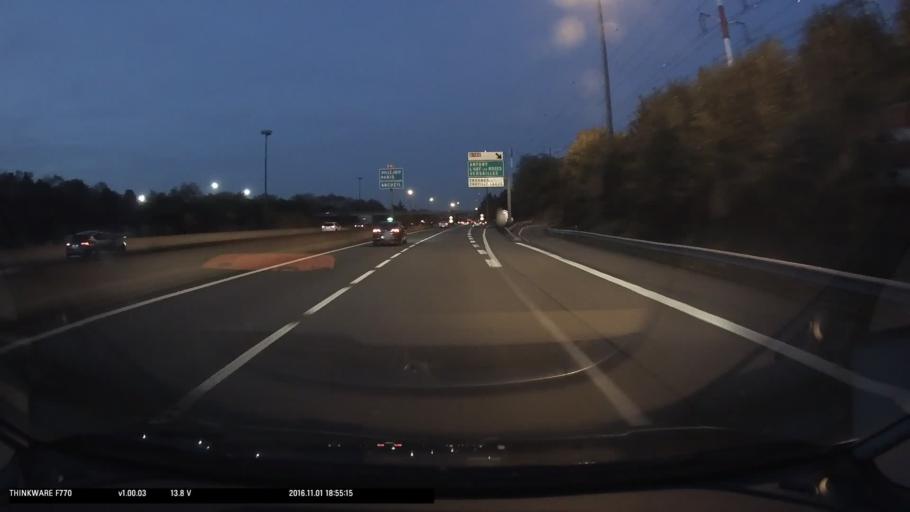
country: FR
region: Ile-de-France
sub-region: Departement du Val-de-Marne
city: Fresnes
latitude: 48.7566
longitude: 2.3351
